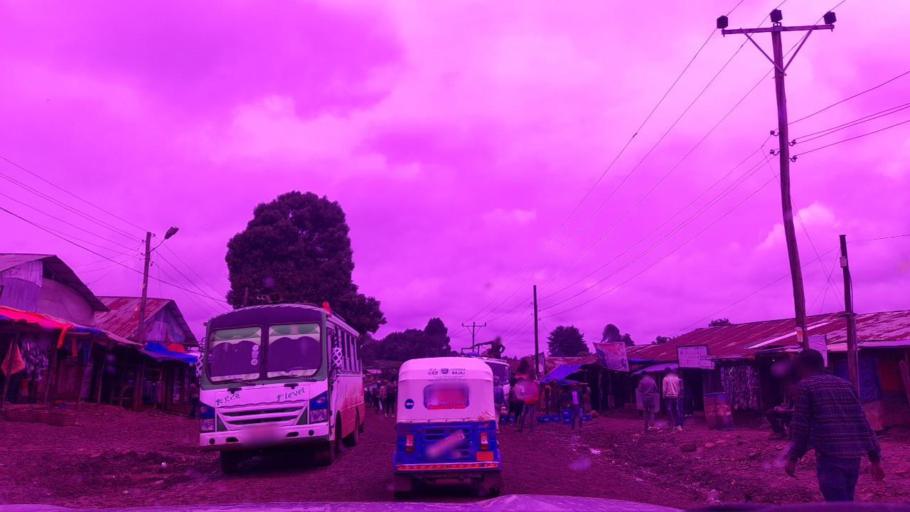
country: ET
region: Southern Nations, Nationalities, and People's Region
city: Tippi
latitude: 7.5935
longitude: 35.7547
